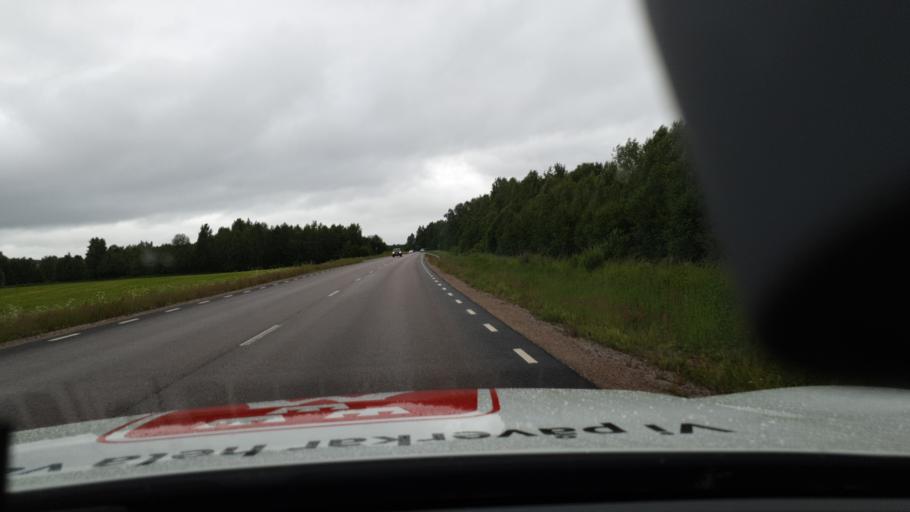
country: SE
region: Norrbotten
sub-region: Overtornea Kommun
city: OEvertornea
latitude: 66.4171
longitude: 23.6259
